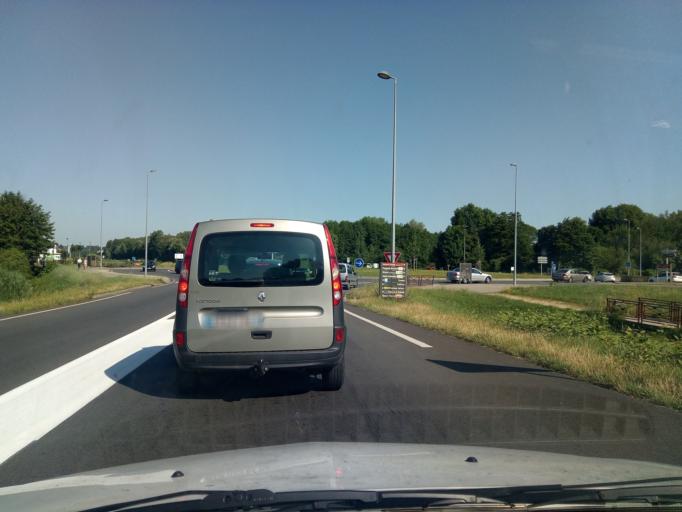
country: FR
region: Rhone-Alpes
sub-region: Departement de l'Isere
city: Bourgoin-Jallieu
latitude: 45.5891
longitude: 5.2587
